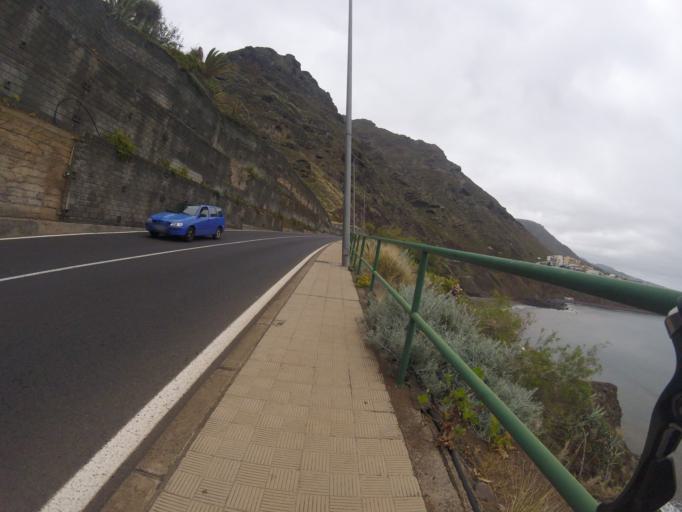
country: ES
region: Canary Islands
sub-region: Provincia de Santa Cruz de Tenerife
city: Tegueste
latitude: 28.5612
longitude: -16.3322
